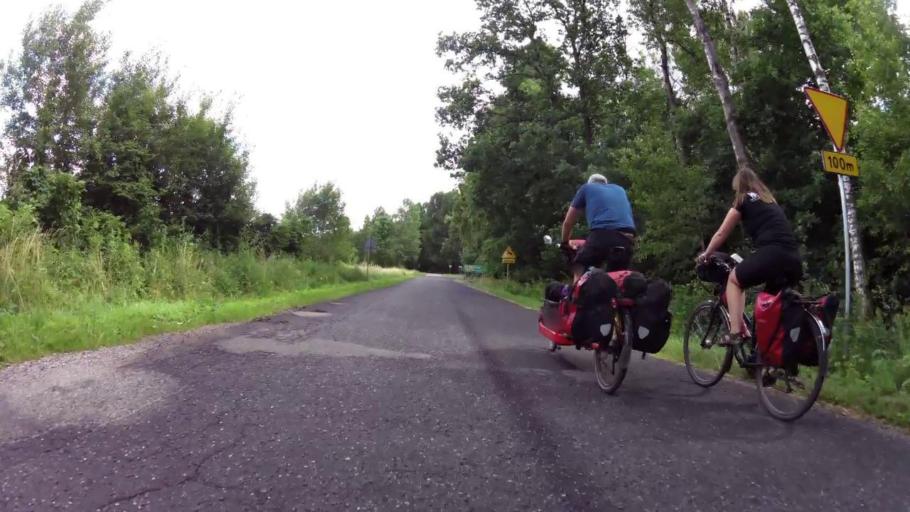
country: PL
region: West Pomeranian Voivodeship
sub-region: Powiat lobeski
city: Lobez
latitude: 53.6575
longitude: 15.5589
